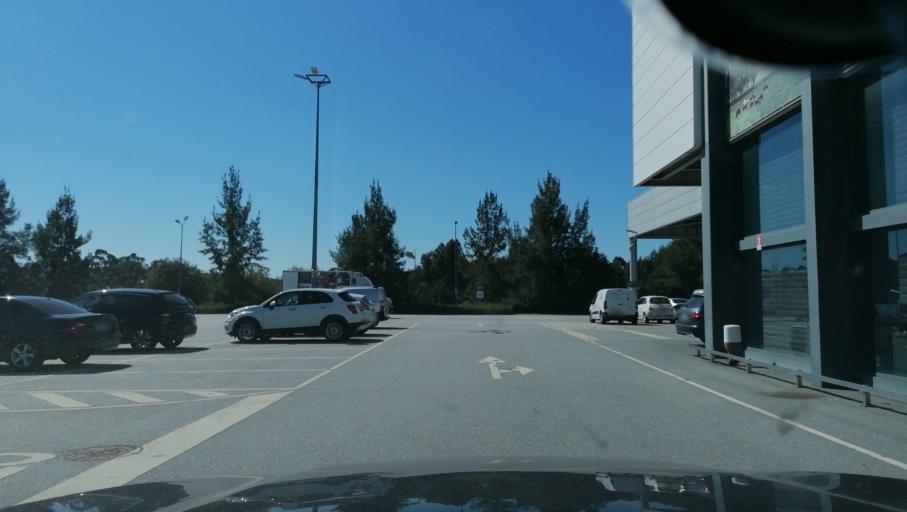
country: PT
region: Aveiro
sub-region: Santa Maria da Feira
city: Feira
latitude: 40.9321
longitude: -8.5273
